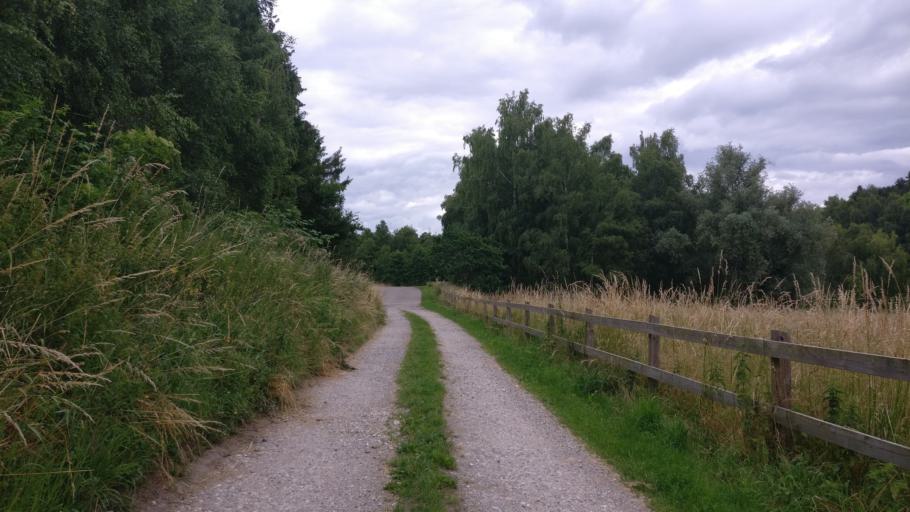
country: DK
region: Capital Region
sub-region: Egedal Kommune
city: Vekso
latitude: 55.7582
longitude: 12.2273
